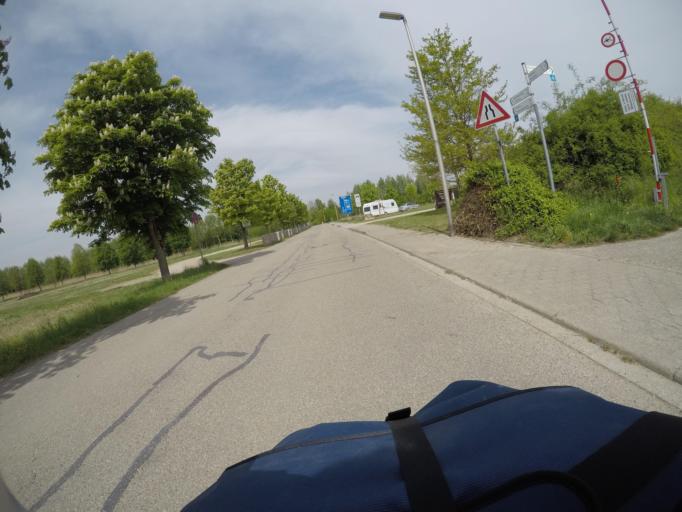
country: DE
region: Baden-Wuerttemberg
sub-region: Karlsruhe Region
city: Schwarzach
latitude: 48.7720
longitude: 8.0424
